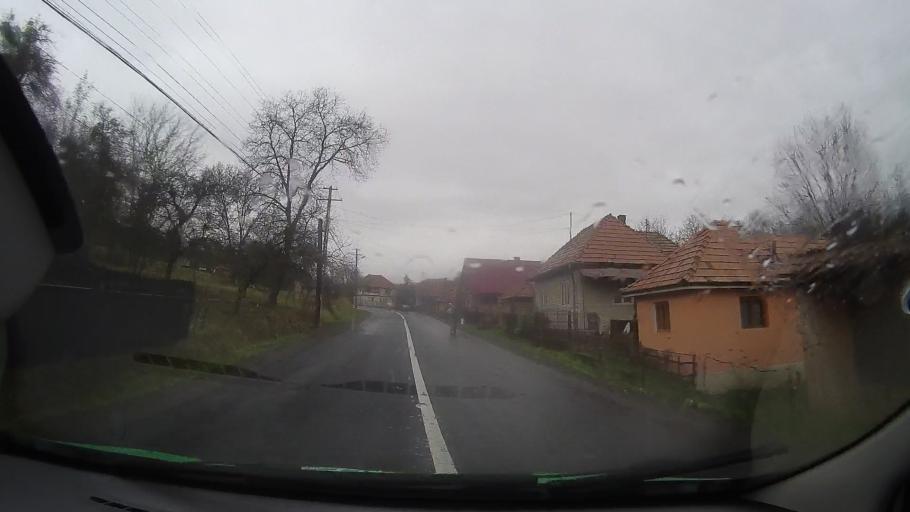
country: RO
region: Mures
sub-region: Comuna Vatava
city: Vatava
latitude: 46.9524
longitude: 24.7628
